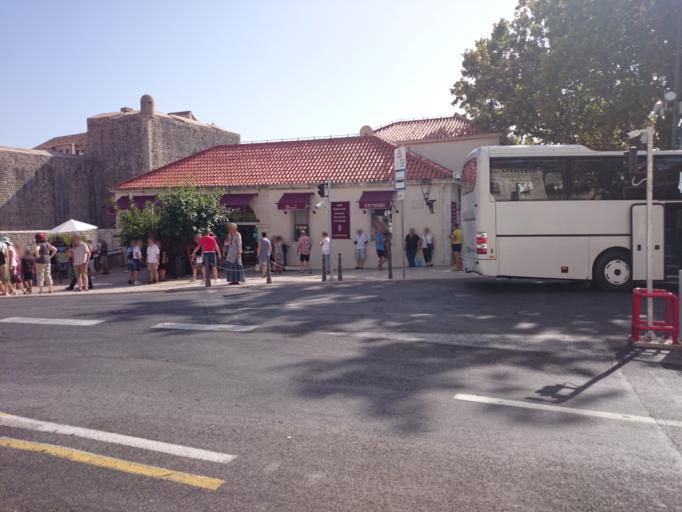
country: HR
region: Dubrovacko-Neretvanska
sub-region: Grad Dubrovnik
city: Dubrovnik
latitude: 42.6420
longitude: 18.1063
